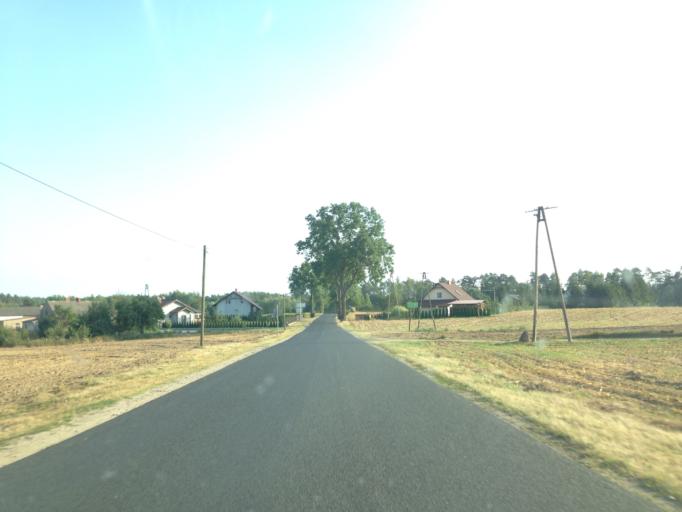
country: PL
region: Kujawsko-Pomorskie
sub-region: Powiat brodnicki
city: Brodnica
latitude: 53.3693
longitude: 19.3754
